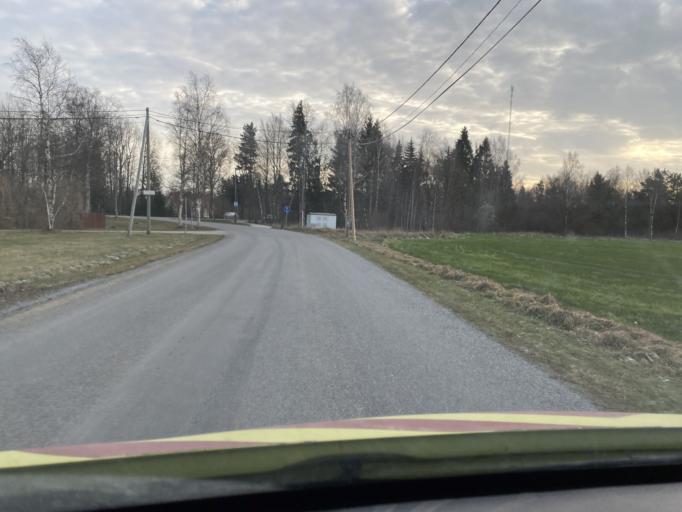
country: EE
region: Jogevamaa
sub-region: Poltsamaa linn
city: Poltsamaa
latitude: 58.6434
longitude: 25.9759
